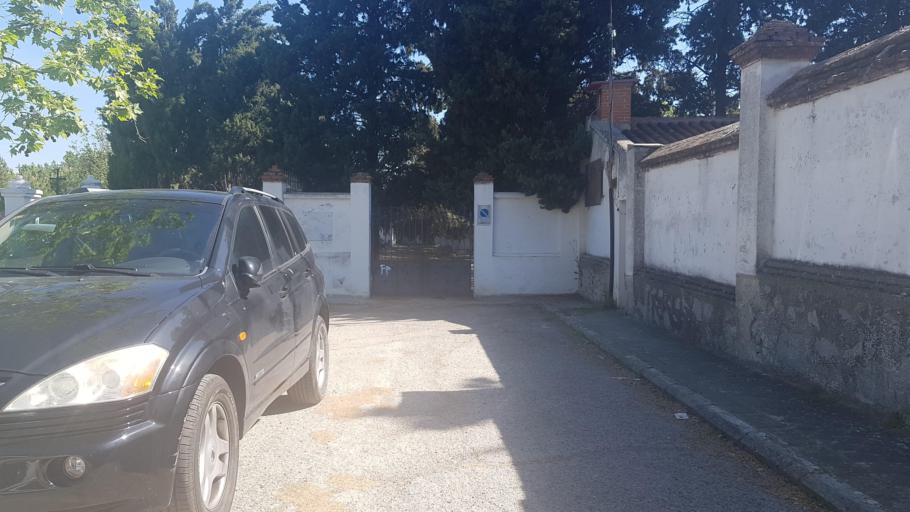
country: ES
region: Madrid
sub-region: Provincia de Madrid
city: Pozuelo de Alarcon
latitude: 40.4660
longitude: -3.7869
